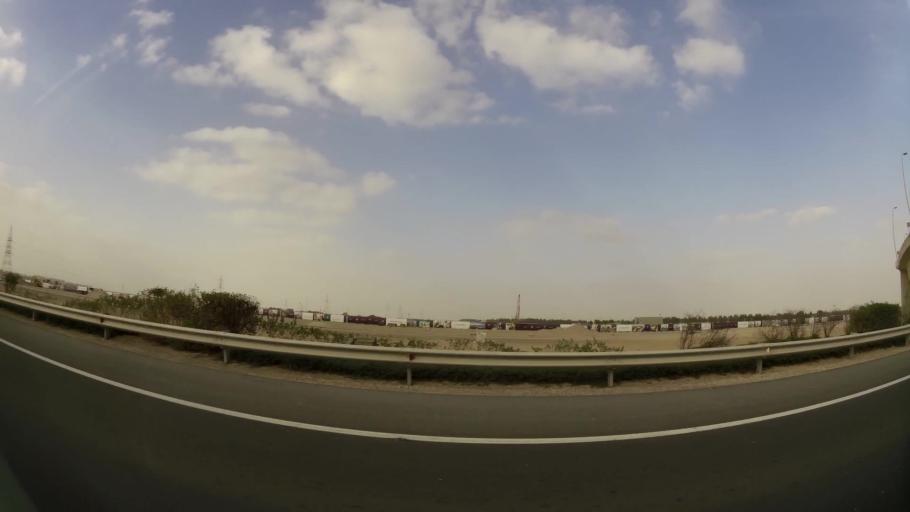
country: AE
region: Abu Dhabi
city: Abu Dhabi
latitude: 24.4953
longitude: 54.6126
